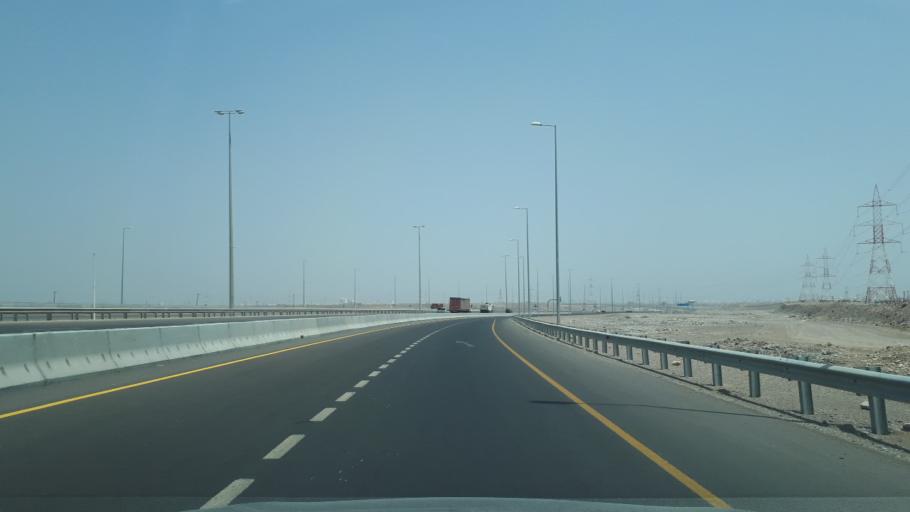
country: OM
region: Muhafazat Masqat
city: As Sib al Jadidah
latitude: 23.6105
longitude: 58.0908
